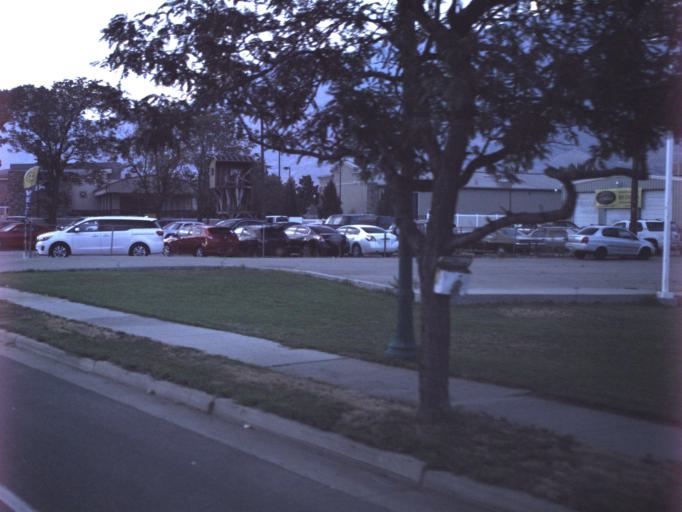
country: US
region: Utah
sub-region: Utah County
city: Orem
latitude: 40.3210
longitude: -111.7053
